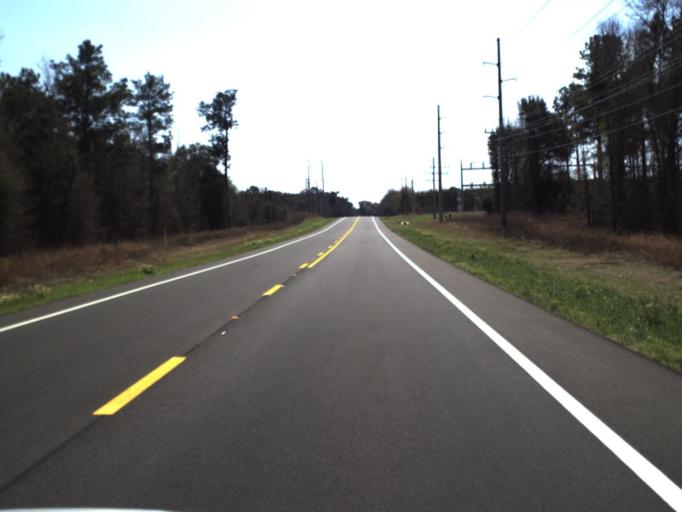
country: US
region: Florida
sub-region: Jackson County
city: Sneads
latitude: 30.7425
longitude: -85.0196
